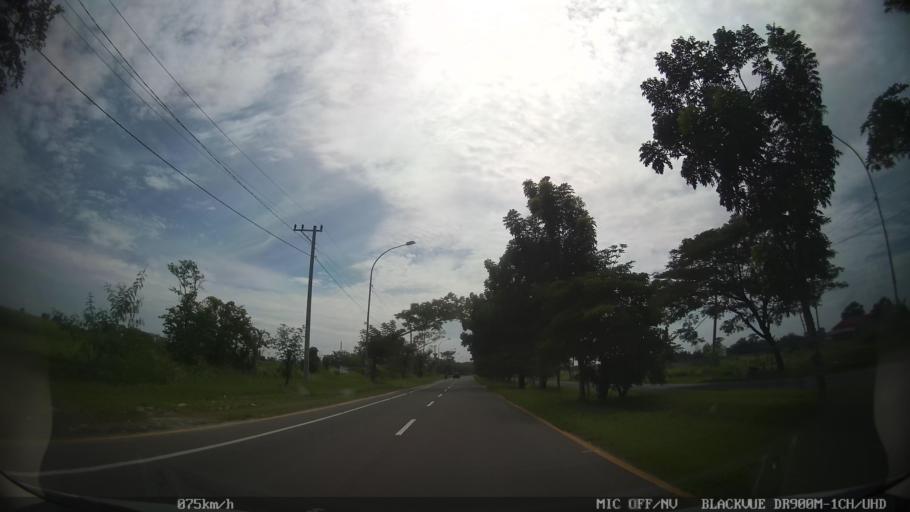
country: ID
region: North Sumatra
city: Percut
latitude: 3.5991
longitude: 98.8188
